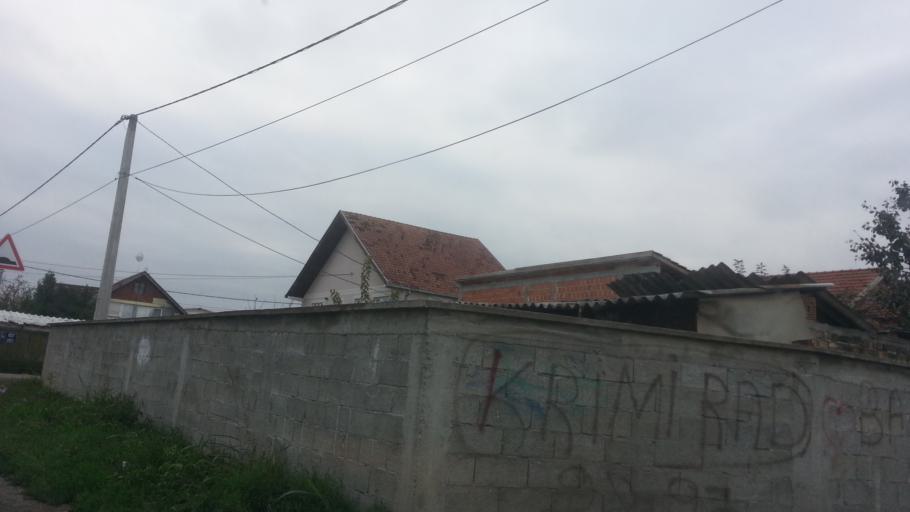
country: RS
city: Novi Banovci
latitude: 44.9160
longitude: 20.2718
